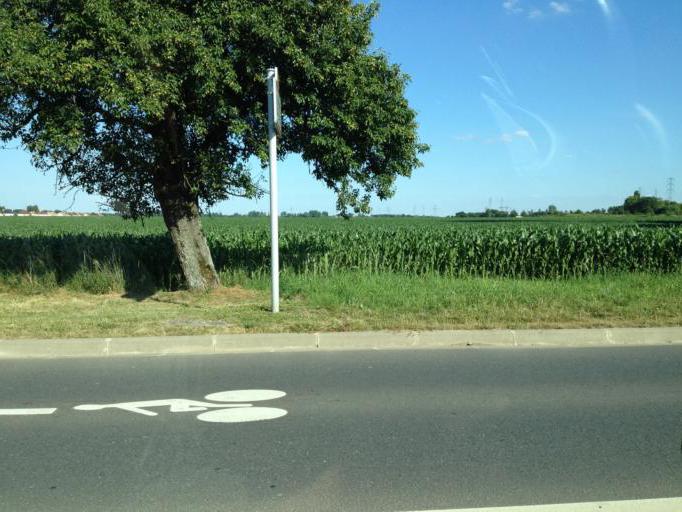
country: FR
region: Ile-de-France
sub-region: Departement des Yvelines
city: Jouy-en-Josas
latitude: 48.7542
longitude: 2.1699
